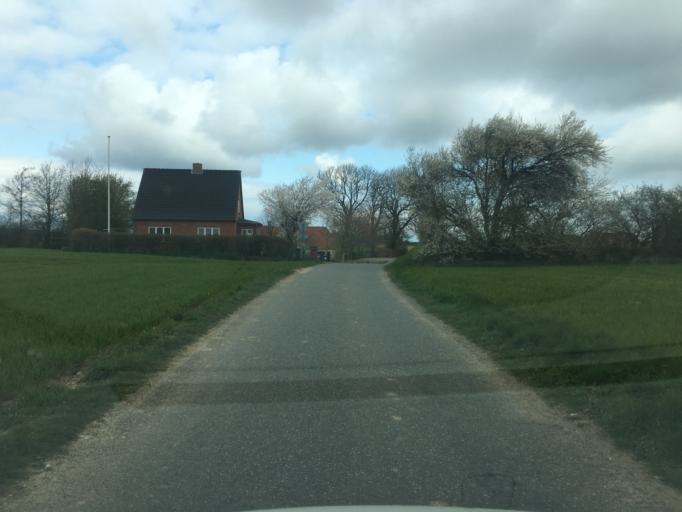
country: DK
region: South Denmark
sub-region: Sonderborg Kommune
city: Grasten
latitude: 54.9833
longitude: 9.5167
